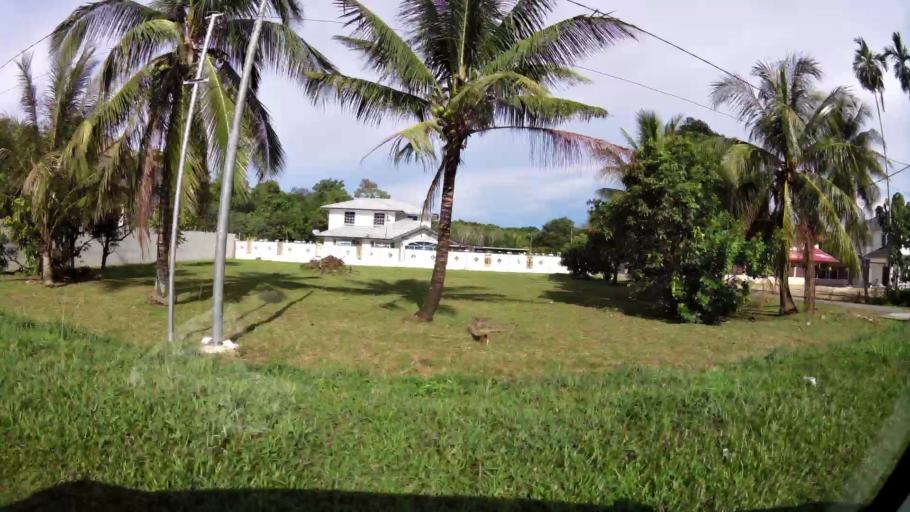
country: BN
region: Brunei and Muara
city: Bandar Seri Begawan
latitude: 4.9820
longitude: 115.0218
